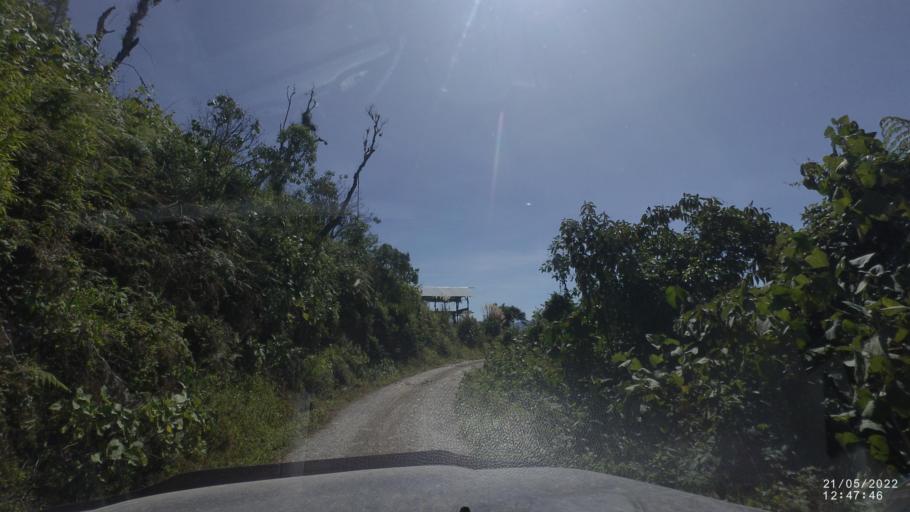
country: BO
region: Cochabamba
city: Colomi
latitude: -17.1823
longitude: -65.9422
